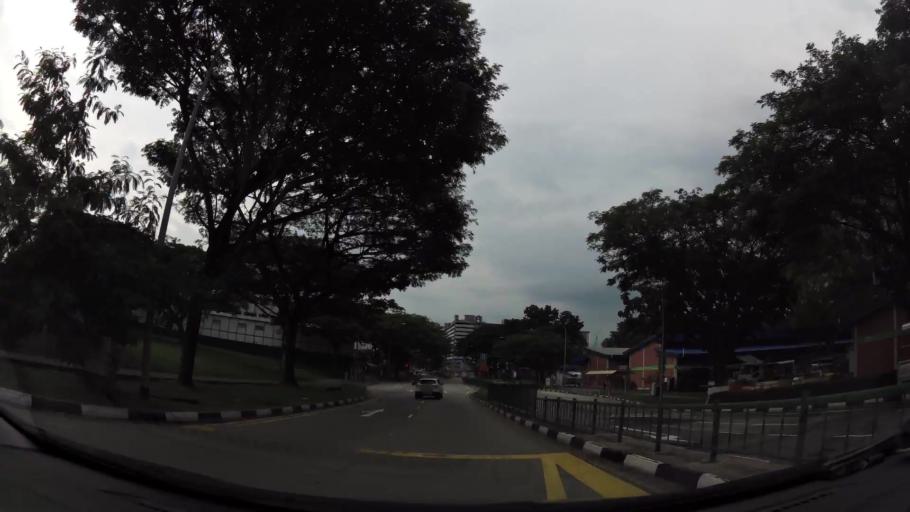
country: SG
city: Singapore
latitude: 1.3192
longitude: 103.8722
